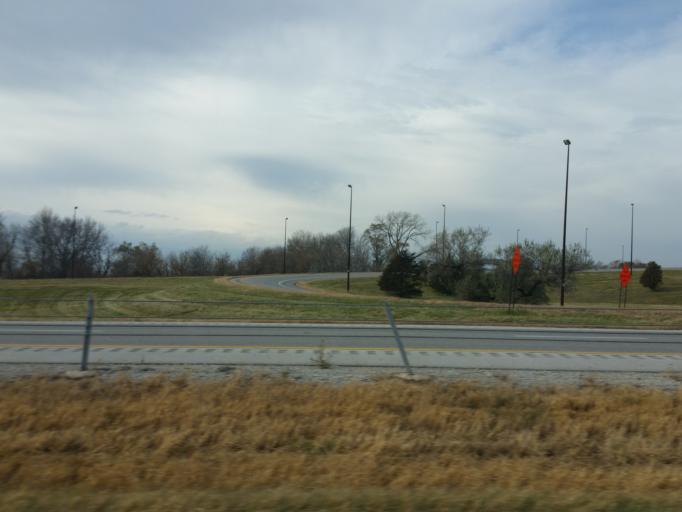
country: US
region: Illinois
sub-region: Rock Island County
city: Moline
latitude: 41.4700
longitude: -90.4948
